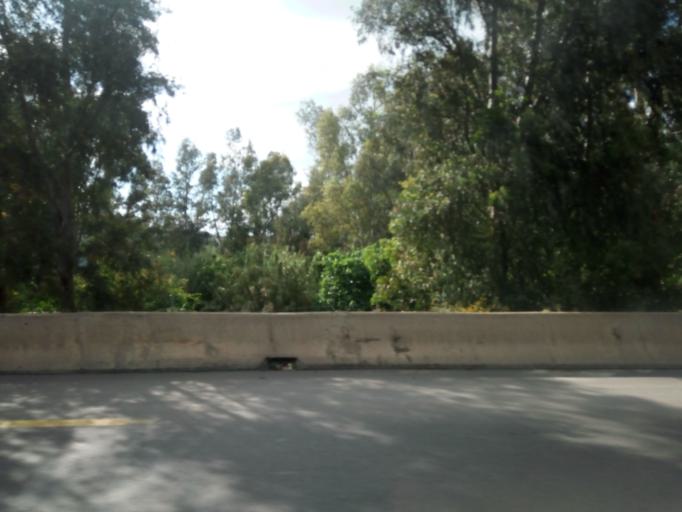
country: DZ
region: Tipaza
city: El Affroun
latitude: 36.4397
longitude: 2.5789
